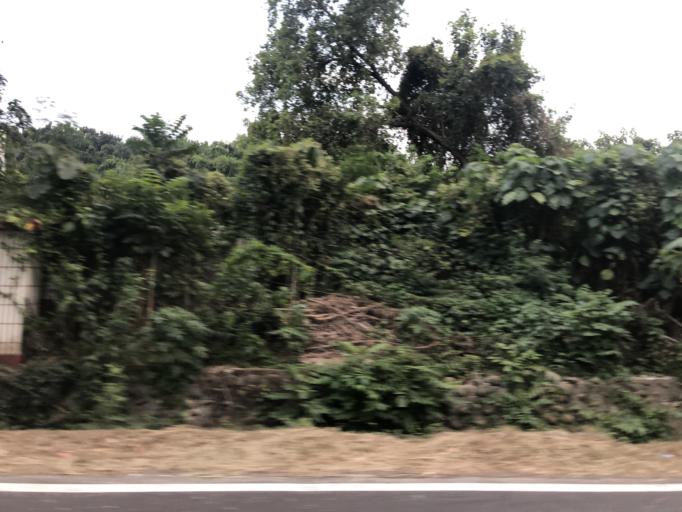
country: TW
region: Taiwan
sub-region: Tainan
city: Tainan
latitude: 23.0254
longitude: 120.3458
